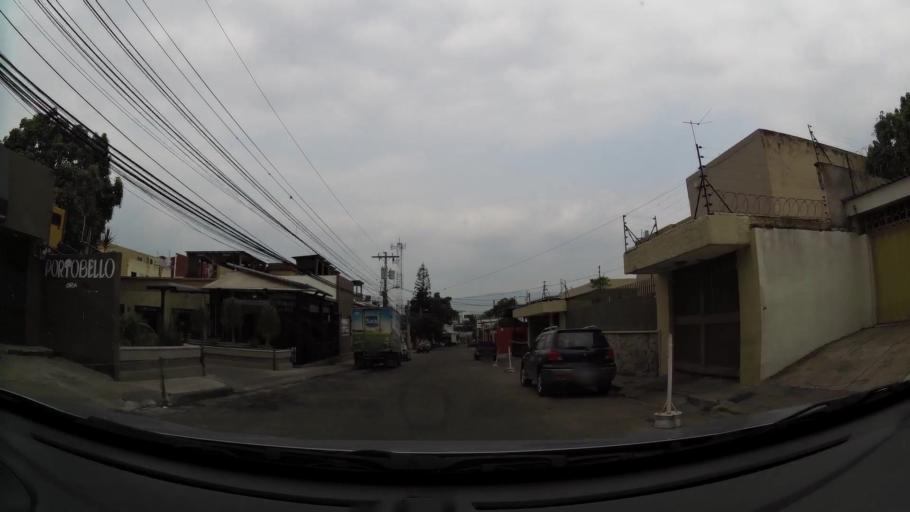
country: HN
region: Francisco Morazan
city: Tegucigalpa
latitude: 14.1004
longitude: -87.1955
